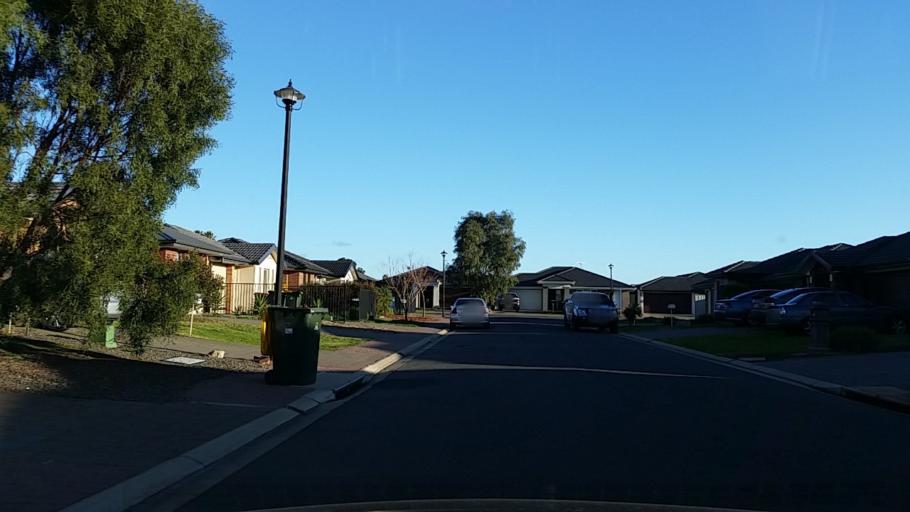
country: AU
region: South Australia
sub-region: Playford
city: Smithfield
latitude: -34.6821
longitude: 138.6839
